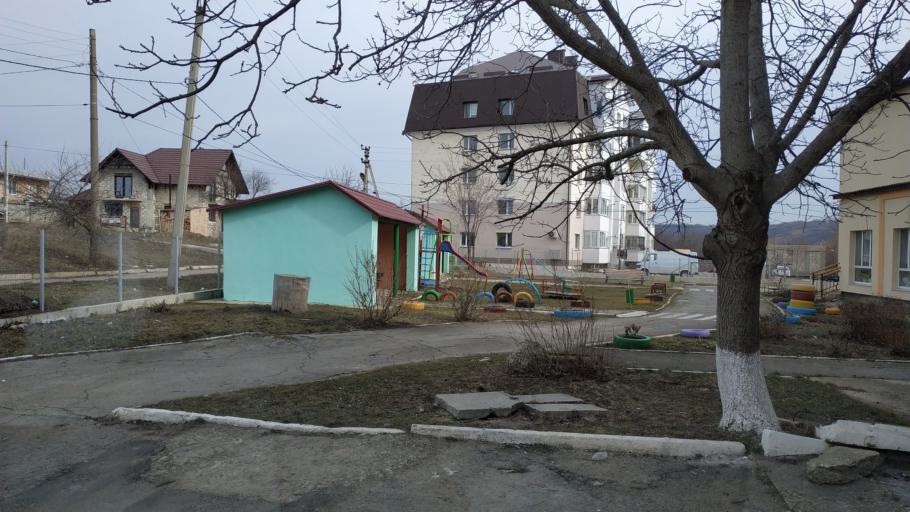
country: MD
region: Chisinau
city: Vatra
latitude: 47.0920
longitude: 28.7610
